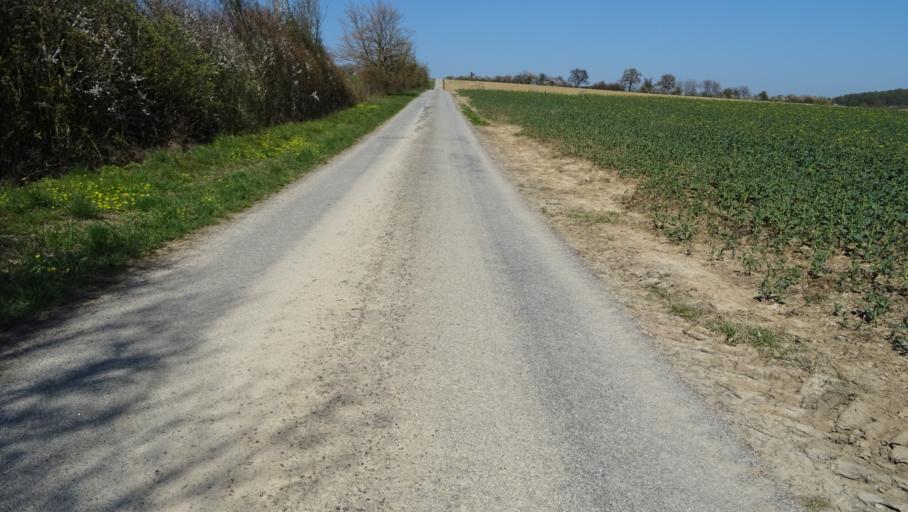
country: DE
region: Baden-Wuerttemberg
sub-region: Karlsruhe Region
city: Limbach
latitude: 49.4209
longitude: 9.2475
